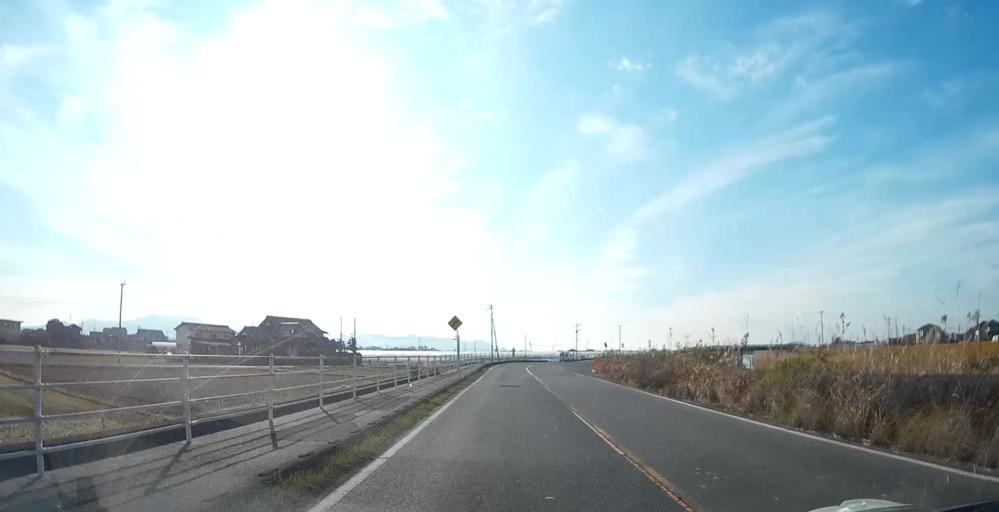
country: JP
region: Kumamoto
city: Uto
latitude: 32.7331
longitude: 130.6608
